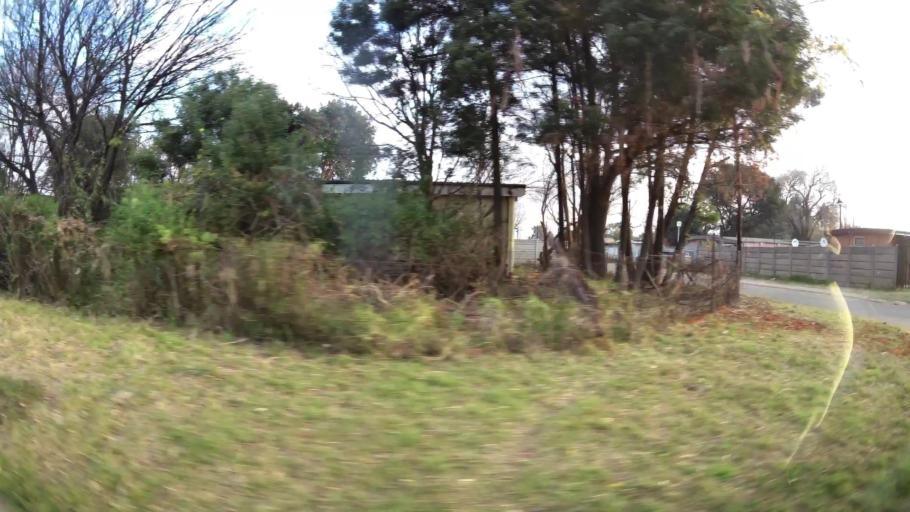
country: ZA
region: Gauteng
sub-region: Ekurhuleni Metropolitan Municipality
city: Benoni
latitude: -26.1575
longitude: 28.3004
